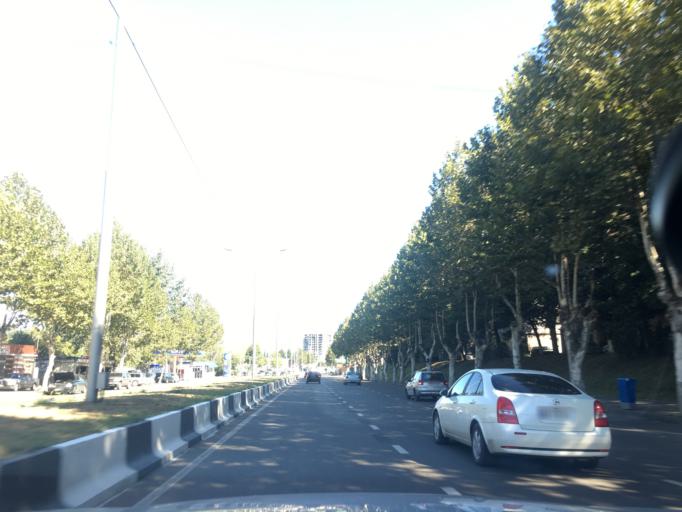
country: GE
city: Zahesi
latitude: 41.7768
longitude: 44.7955
